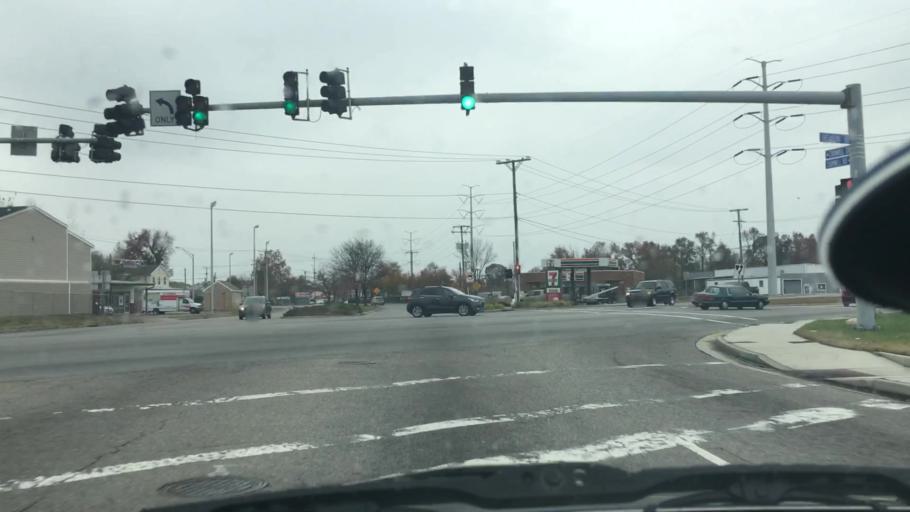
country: US
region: Virginia
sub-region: City of Norfolk
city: Norfolk
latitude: 36.8759
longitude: -76.2520
